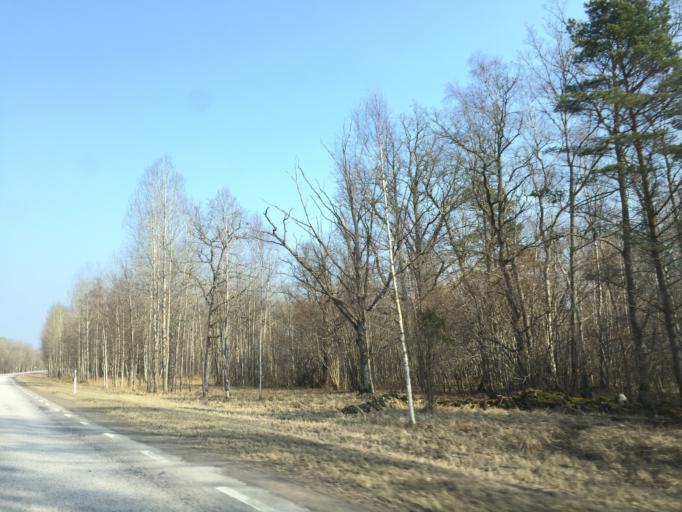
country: EE
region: Saare
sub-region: Kuressaare linn
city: Kuressaare
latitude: 58.3966
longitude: 22.7558
